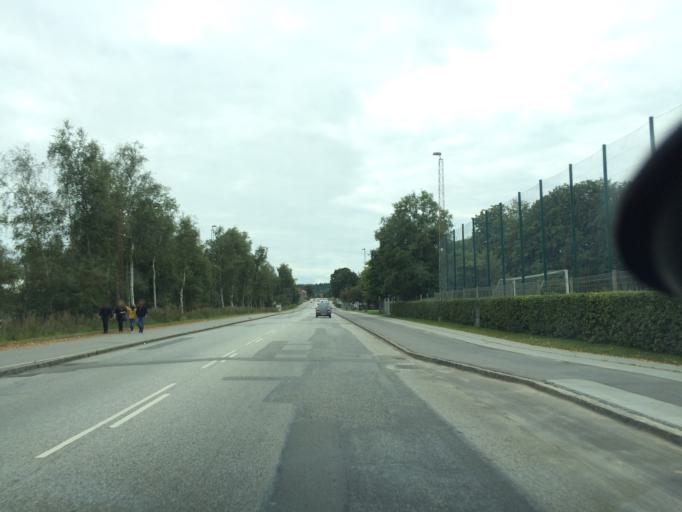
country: DK
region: South Denmark
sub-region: Aabenraa Kommune
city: Aabenraa
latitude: 55.0383
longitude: 9.4065
